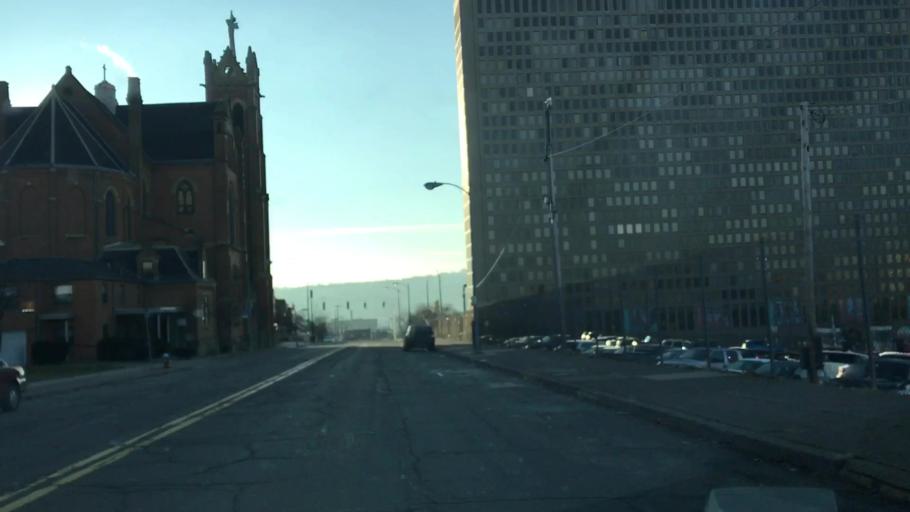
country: US
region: Pennsylvania
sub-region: Allegheny County
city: Pittsburgh
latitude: 40.4420
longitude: -79.9868
